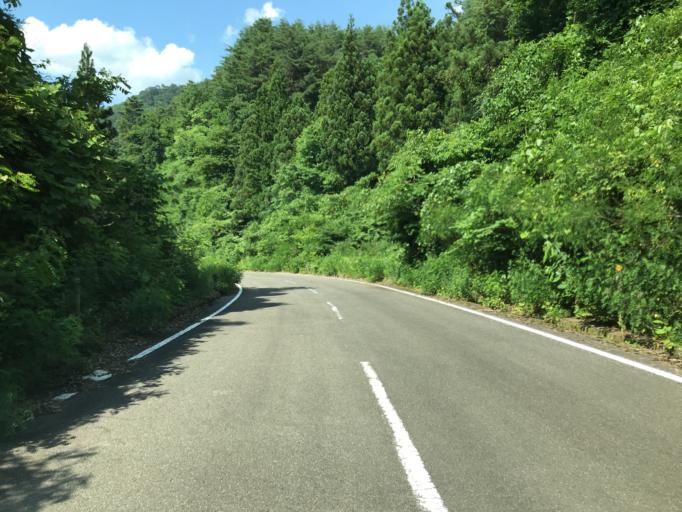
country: JP
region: Fukushima
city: Yanagawamachi-saiwaicho
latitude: 37.7806
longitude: 140.6695
